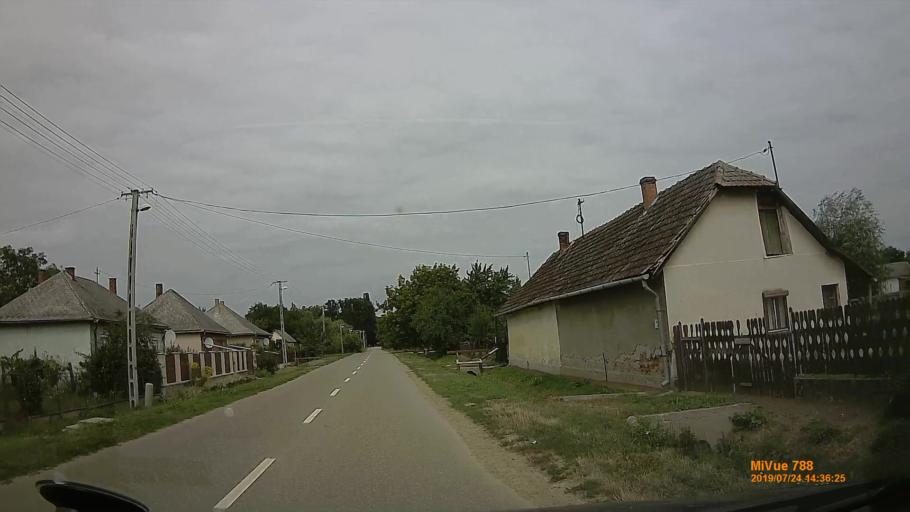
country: HU
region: Szabolcs-Szatmar-Bereg
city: Mandok
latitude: 48.3214
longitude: 22.2629
